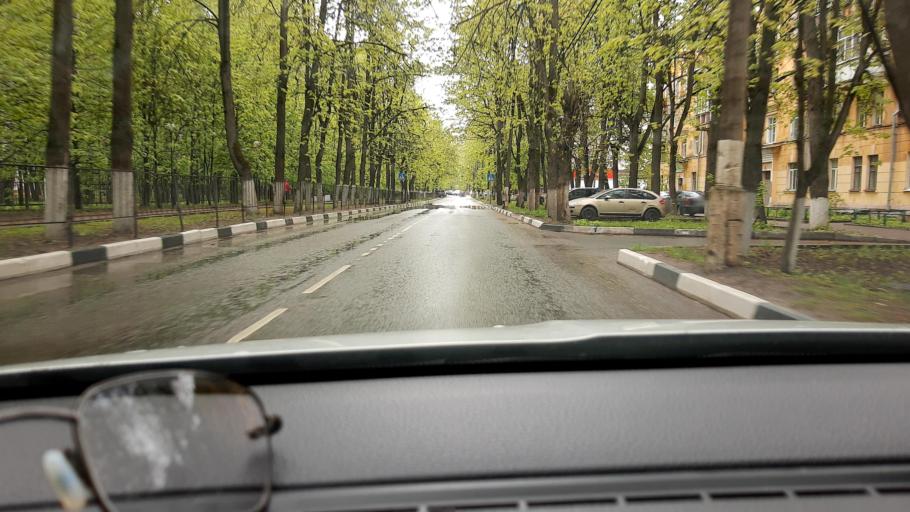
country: RU
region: Moskovskaya
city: Krasnogorsk
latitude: 55.8257
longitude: 37.3315
